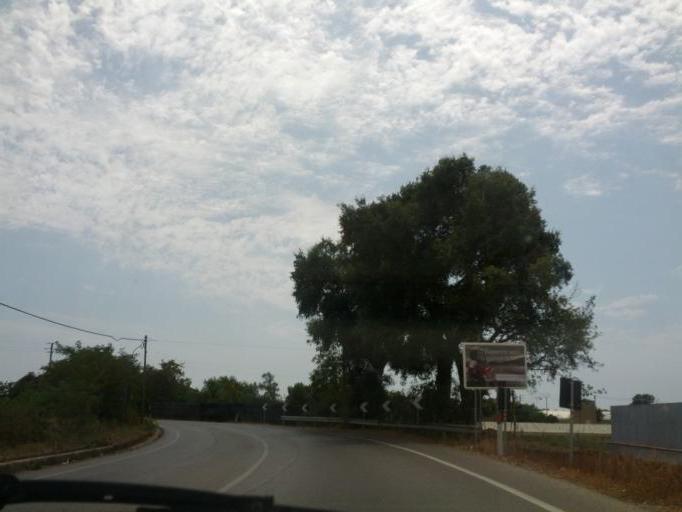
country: IT
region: Latium
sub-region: Provincia di Latina
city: Sperlonga
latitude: 41.2972
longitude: 13.3965
